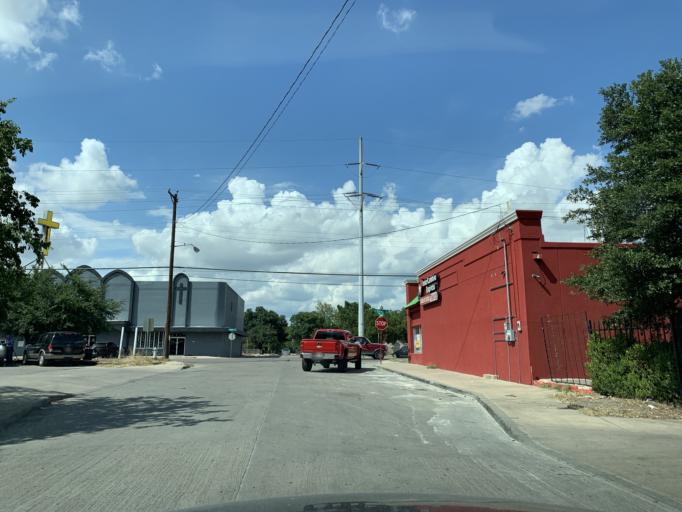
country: US
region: Texas
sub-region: Dallas County
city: Cockrell Hill
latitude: 32.7491
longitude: -96.8727
